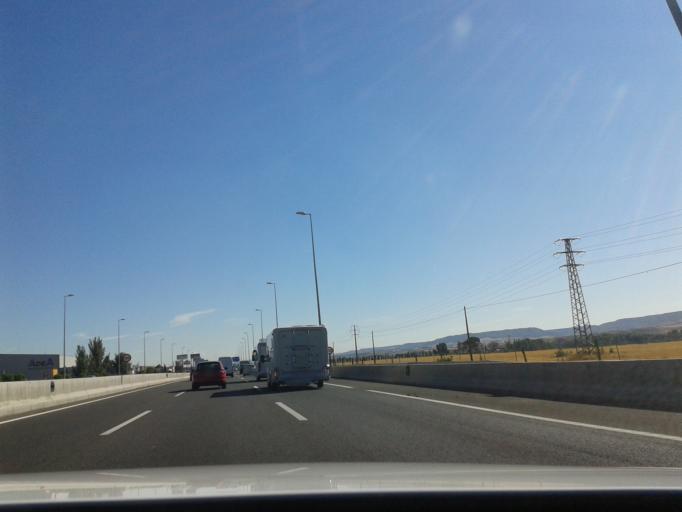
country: ES
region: Castille-La Mancha
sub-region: Provincia de Guadalajara
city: Azuqueca de Henares
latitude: 40.5370
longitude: -3.2835
